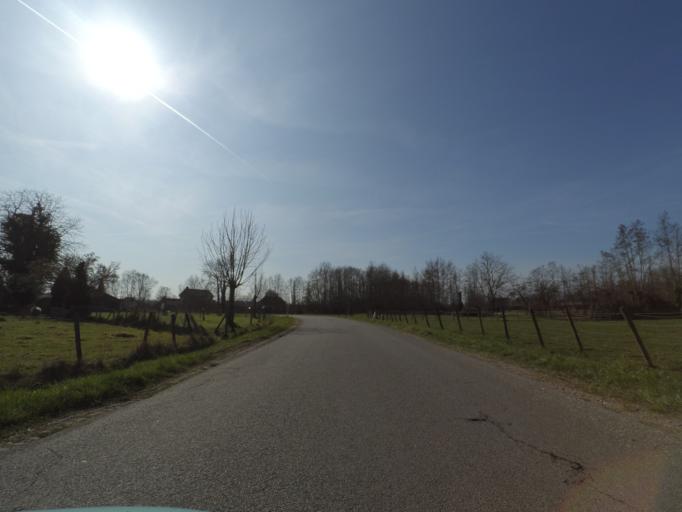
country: NL
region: Gelderland
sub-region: Gemeente Barneveld
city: Zwartebroek
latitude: 52.1826
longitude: 5.5070
